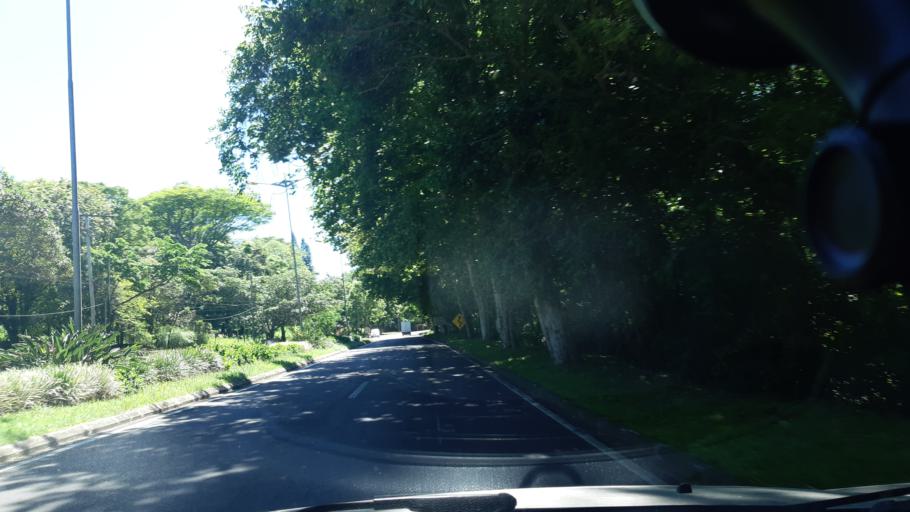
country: BR
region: Rio Grande do Sul
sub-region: Ivoti
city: Ivoti
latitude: -29.6249
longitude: -51.1356
